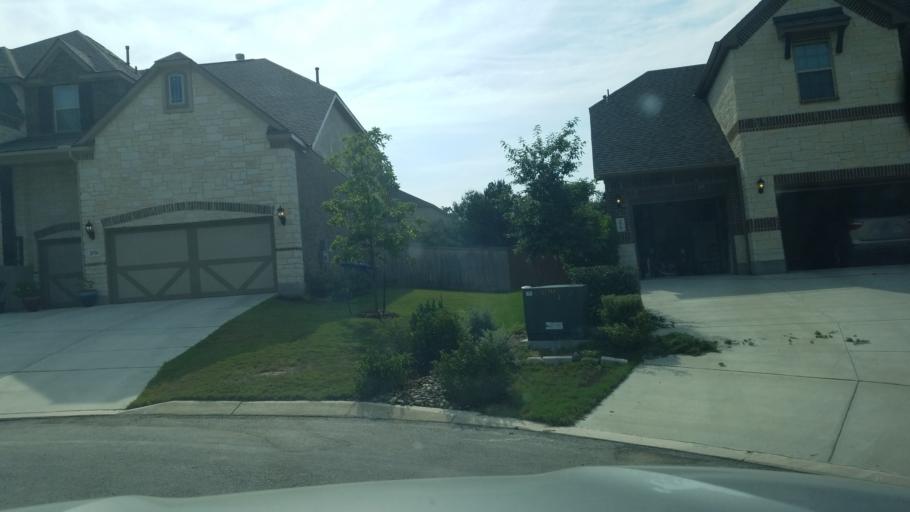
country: US
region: Texas
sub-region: Bexar County
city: Scenic Oaks
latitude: 29.7240
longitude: -98.6606
